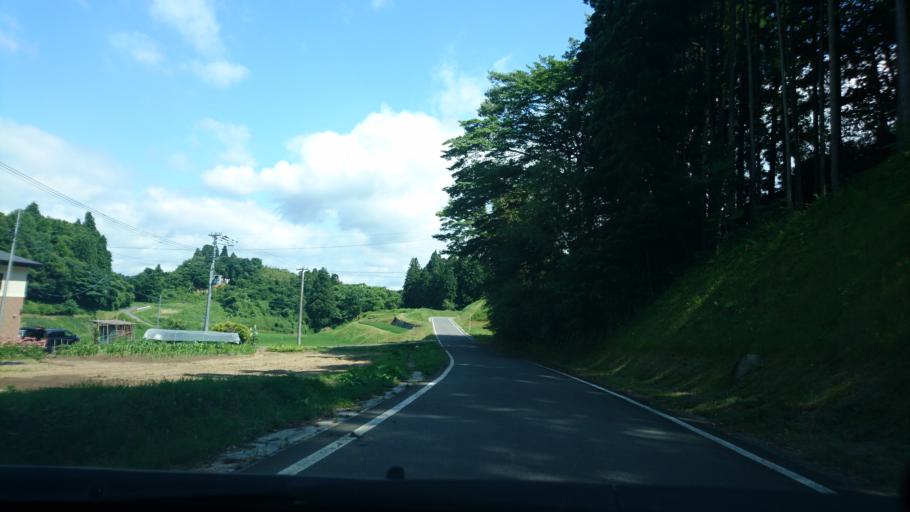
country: JP
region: Iwate
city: Ichinoseki
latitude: 38.9808
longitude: 141.1944
